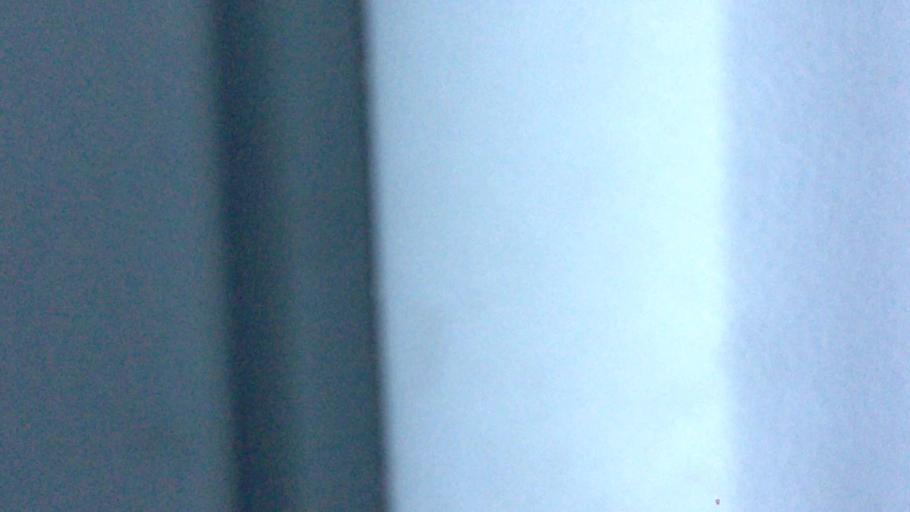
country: US
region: New York
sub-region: Dutchess County
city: Rhinebeck
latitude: 41.9588
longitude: -73.9213
